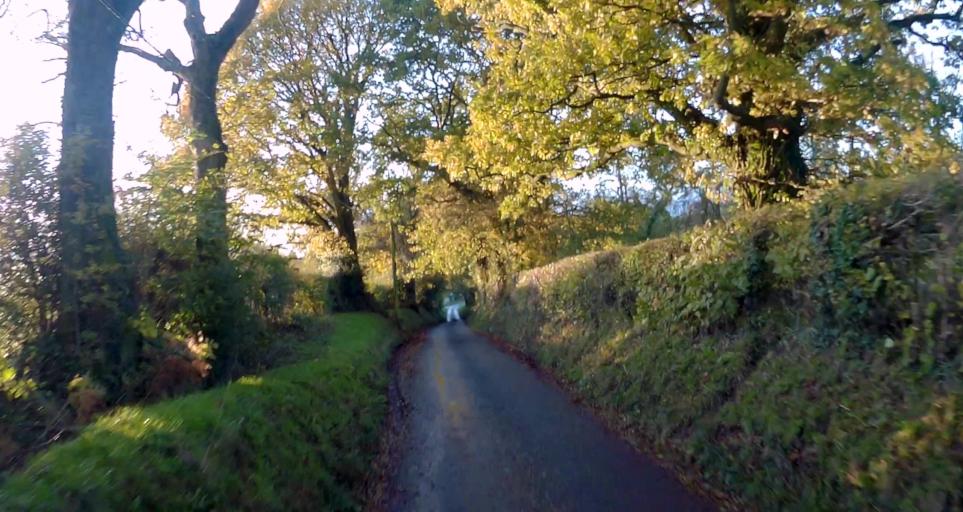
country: GB
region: England
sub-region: Hampshire
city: Basingstoke
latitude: 51.2079
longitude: -1.0833
